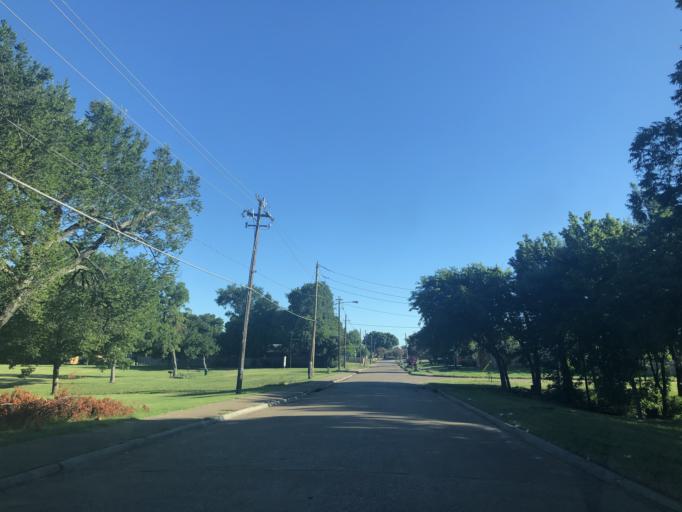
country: US
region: Texas
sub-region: Dallas County
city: Duncanville
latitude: 32.6415
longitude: -96.9437
